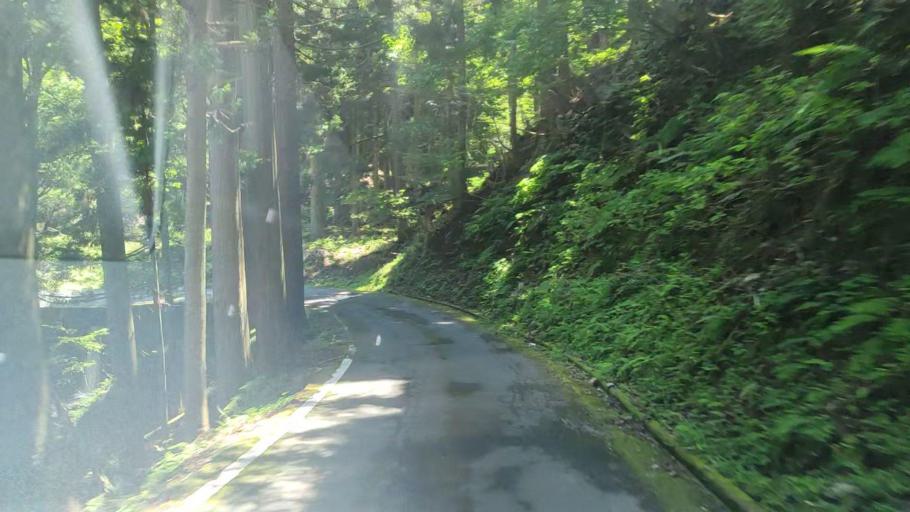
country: JP
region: Fukui
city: Ono
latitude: 35.7096
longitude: 136.5826
